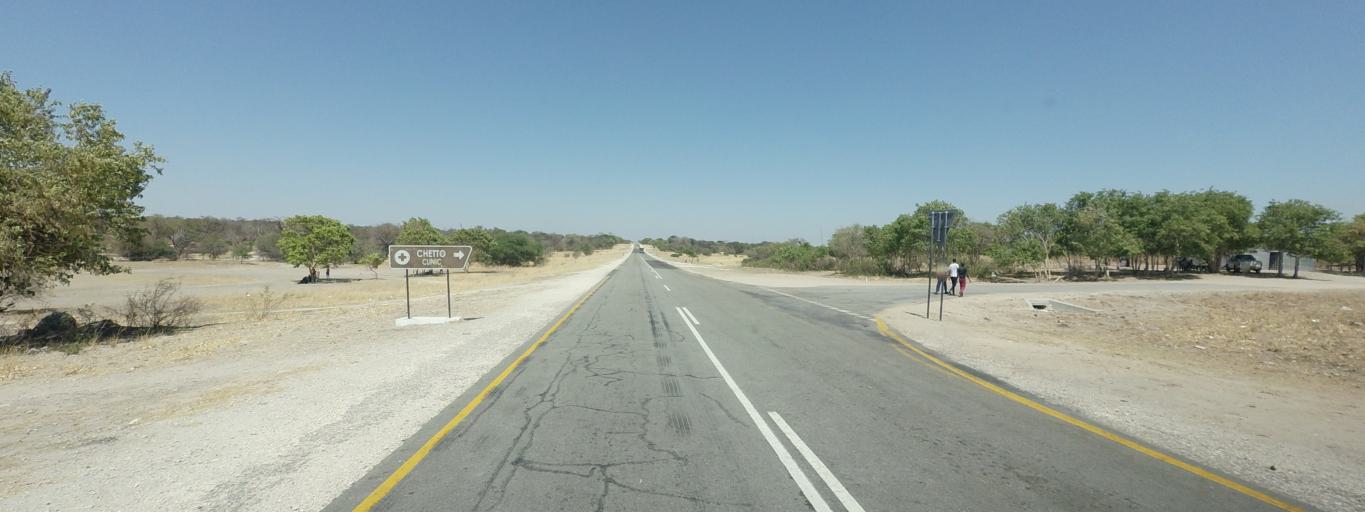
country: BW
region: North West
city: Shakawe
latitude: -17.9574
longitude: 22.5597
